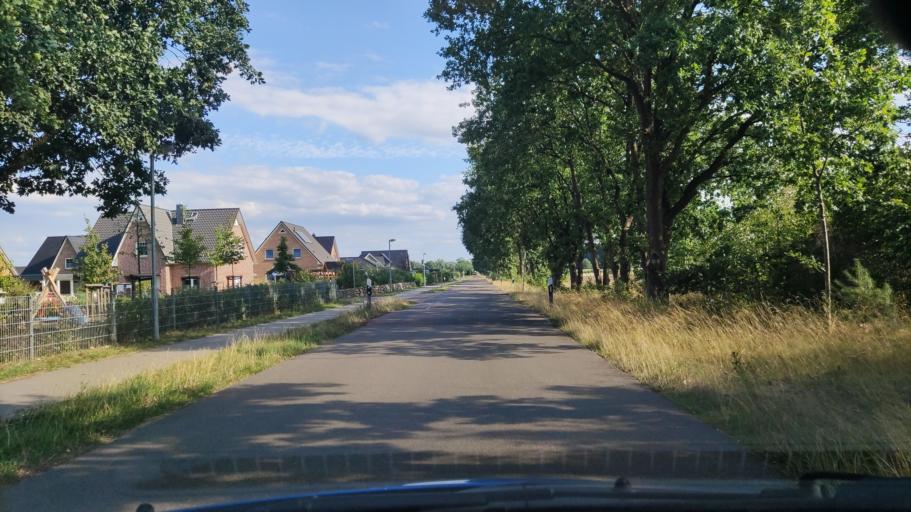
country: DE
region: Lower Saxony
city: Handorf
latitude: 53.3351
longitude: 10.3519
